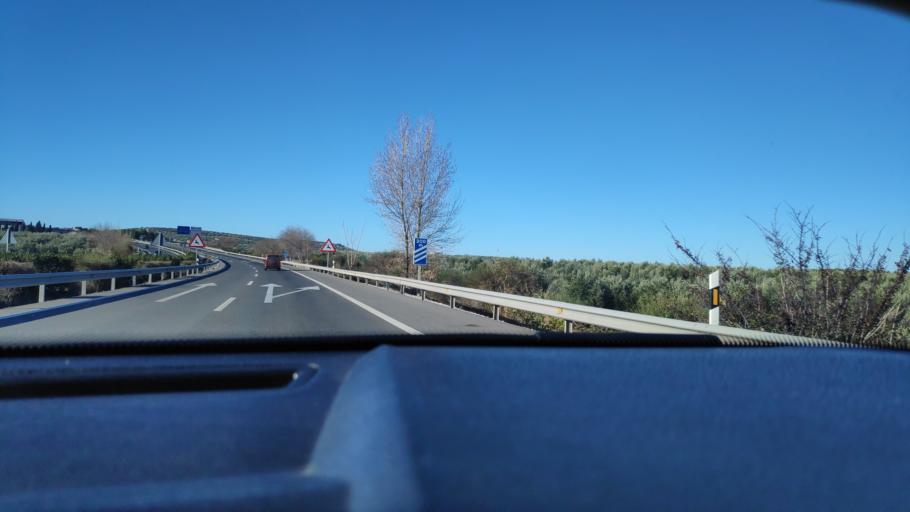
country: ES
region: Andalusia
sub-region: Provincia de Jaen
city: Torre del Campo
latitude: 37.7802
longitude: -3.8974
